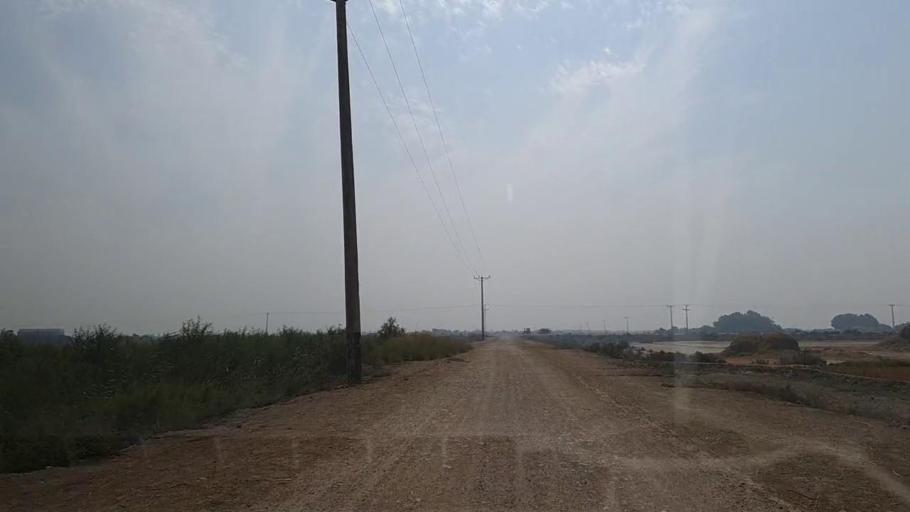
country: PK
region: Sindh
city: Mirpur Batoro
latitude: 24.5994
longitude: 68.2149
